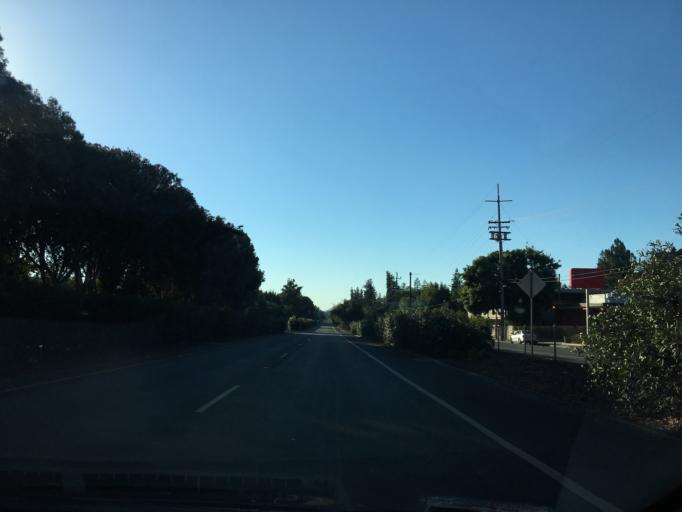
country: US
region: California
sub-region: Santa Clara County
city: Loyola
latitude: 37.3543
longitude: -122.0895
